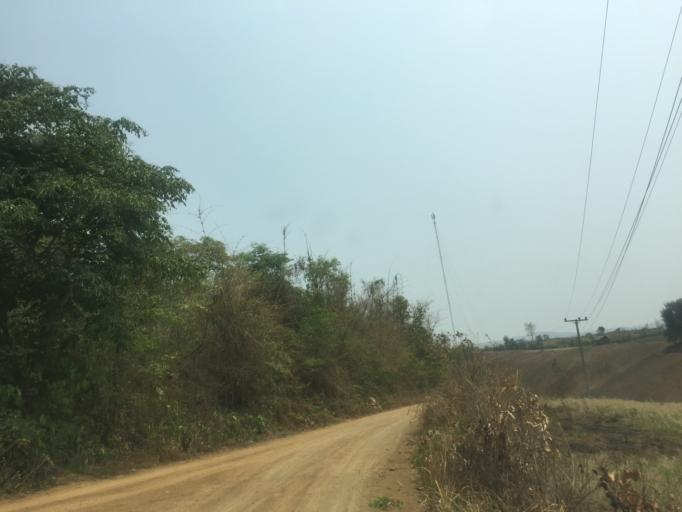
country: LA
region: Xiagnabouli
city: Muang Kenthao
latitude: 17.7964
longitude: 101.2607
